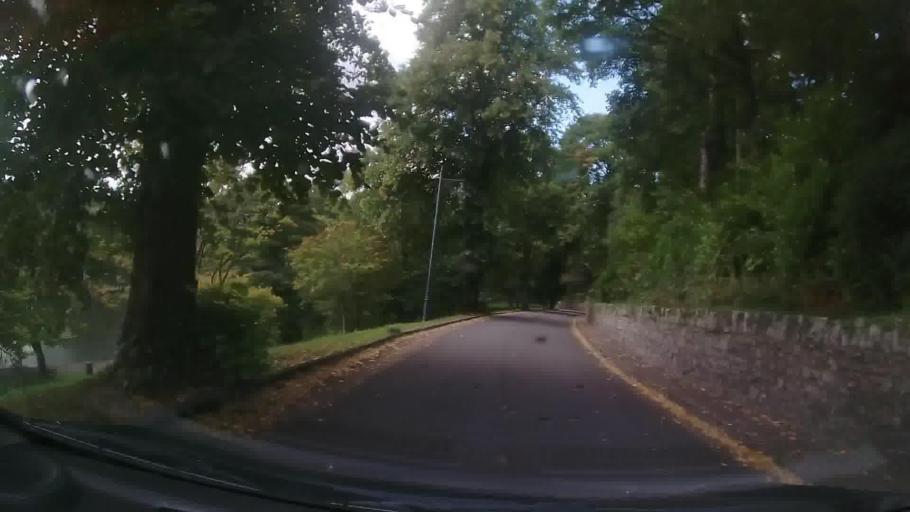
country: GB
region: Wales
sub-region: Merthyr Tydfil County Borough
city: Merthyr Tydfil
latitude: 51.7571
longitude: -3.3920
